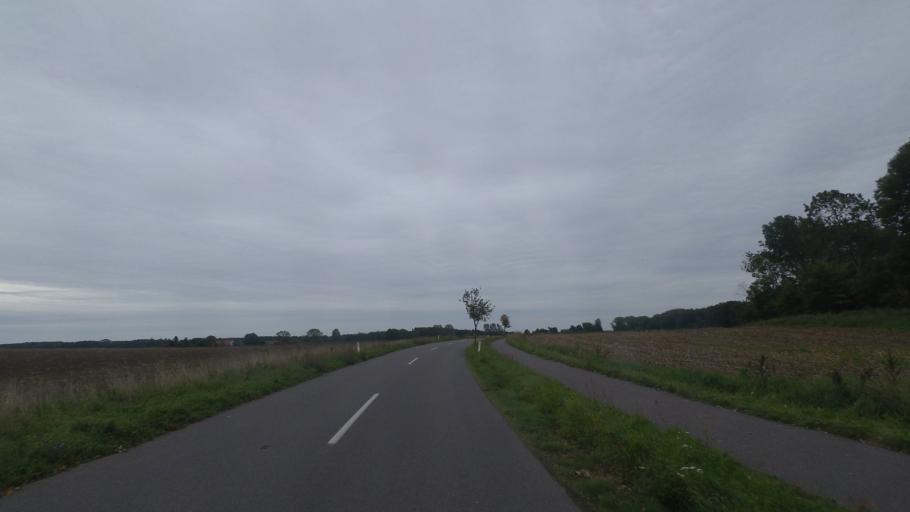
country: DK
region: Capital Region
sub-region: Bornholm Kommune
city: Akirkeby
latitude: 55.0073
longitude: 14.9974
